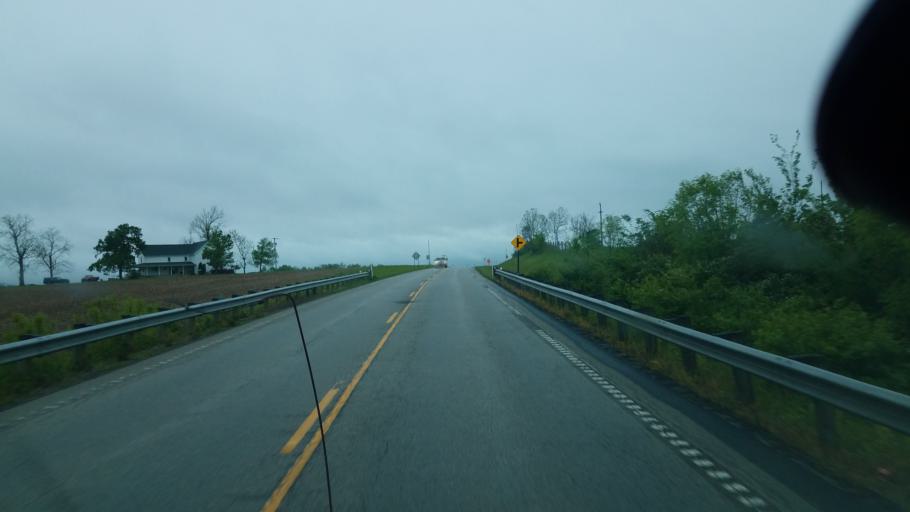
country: US
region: Ohio
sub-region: Highland County
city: Leesburg
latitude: 39.3034
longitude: -83.5796
